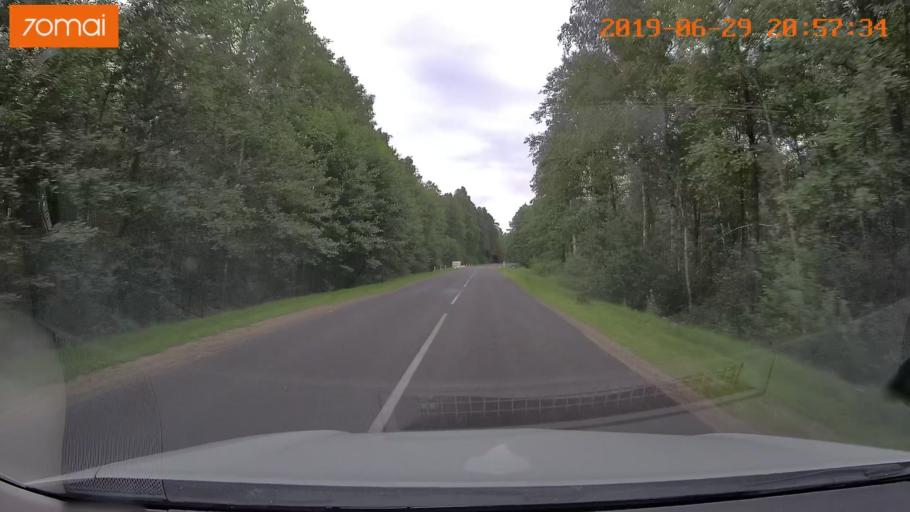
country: BY
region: Brest
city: Hantsavichy
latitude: 52.7207
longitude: 26.3720
